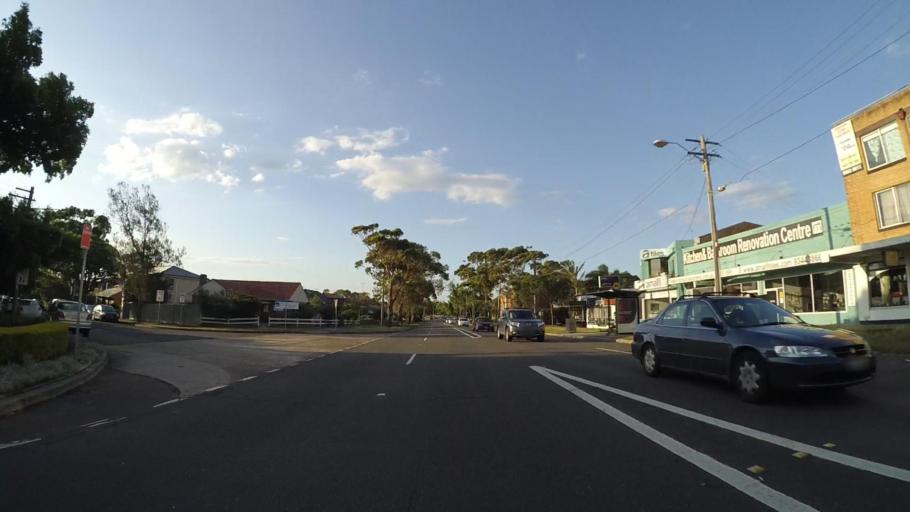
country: AU
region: New South Wales
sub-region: Randwick
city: Daceyville
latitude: -33.9335
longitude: 151.2303
